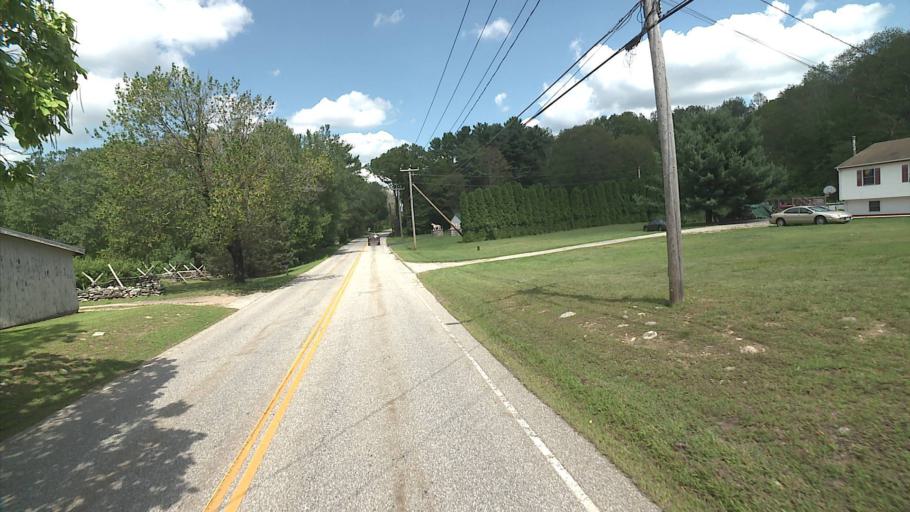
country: US
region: Connecticut
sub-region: Windham County
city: Windham
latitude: 41.7259
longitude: -72.1669
